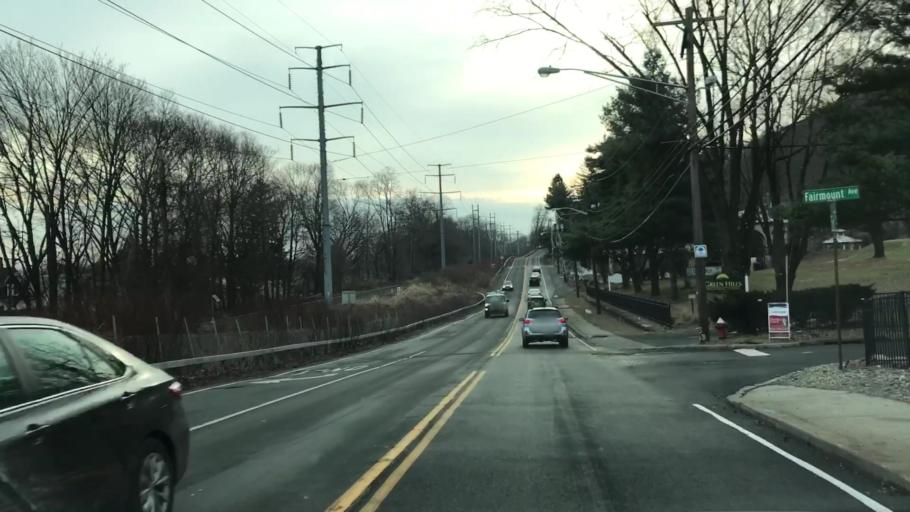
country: US
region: New York
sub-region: Rockland County
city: Haverstraw
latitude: 41.1938
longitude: -73.9680
